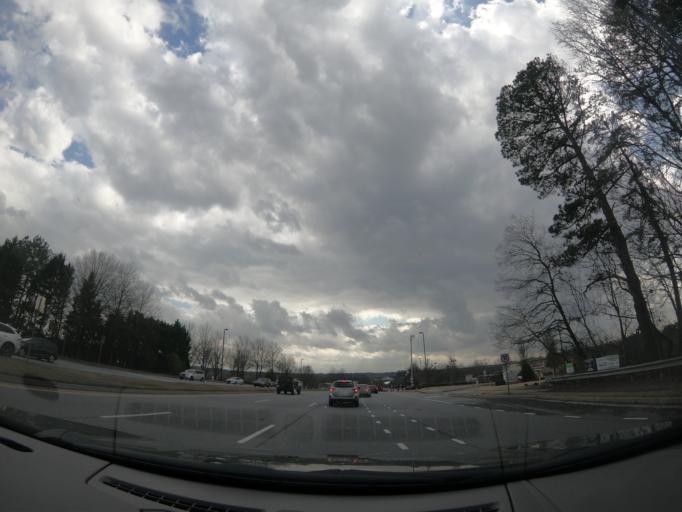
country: US
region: Georgia
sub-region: Fulton County
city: Alpharetta
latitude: 34.0529
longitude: -84.2855
